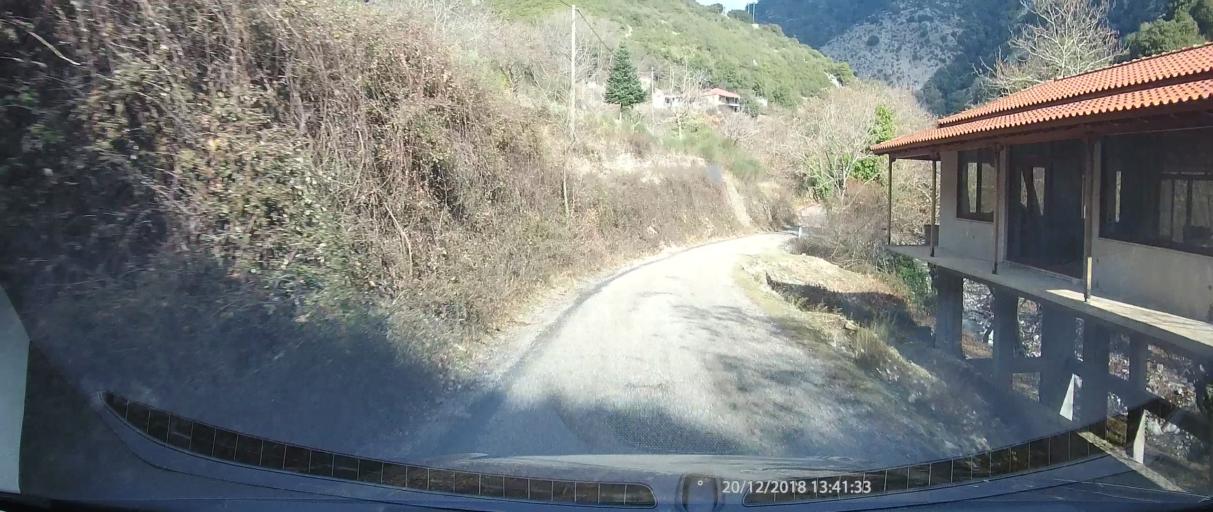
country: GR
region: West Greece
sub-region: Nomos Aitolias kai Akarnanias
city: Thermo
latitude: 38.6494
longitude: 21.6147
